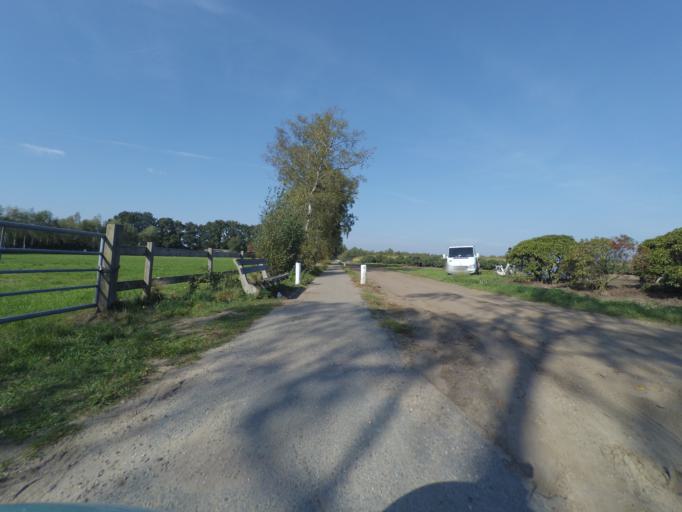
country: NL
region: Gelderland
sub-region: Gemeente Ede
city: Otterlo
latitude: 52.1092
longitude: 5.7596
